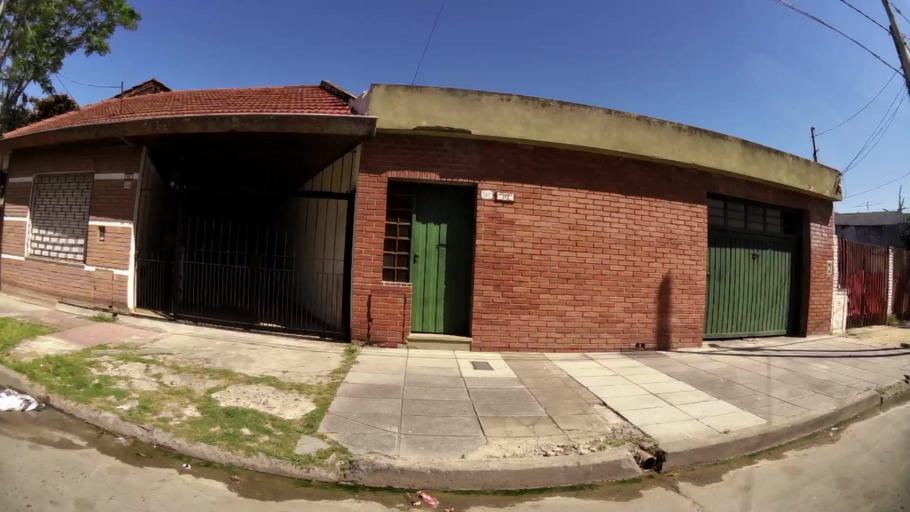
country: AR
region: Buenos Aires
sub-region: Partido de General San Martin
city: General San Martin
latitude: -34.5501
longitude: -58.5672
